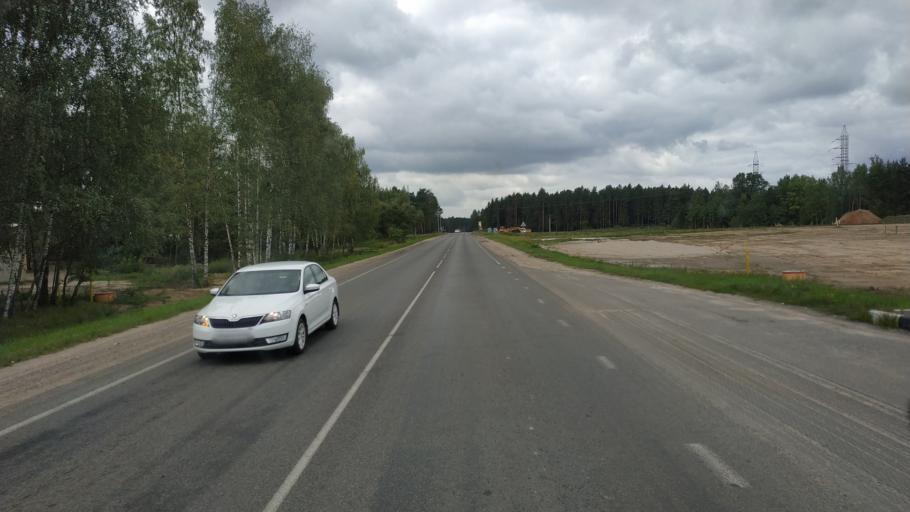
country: BY
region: Mogilev
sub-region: Mahilyowski Rayon
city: Veyno
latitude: 53.8754
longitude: 30.4306
